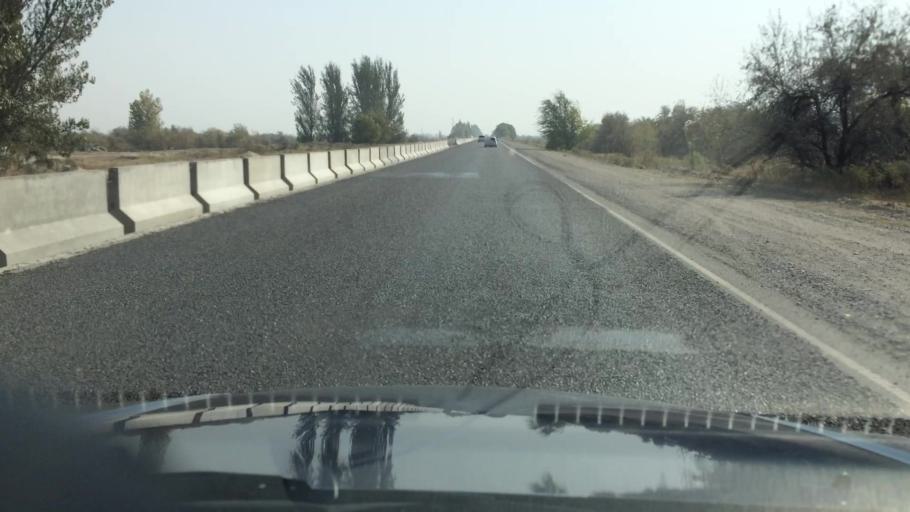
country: KG
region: Chuy
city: Kant
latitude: 42.9728
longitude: 74.8984
